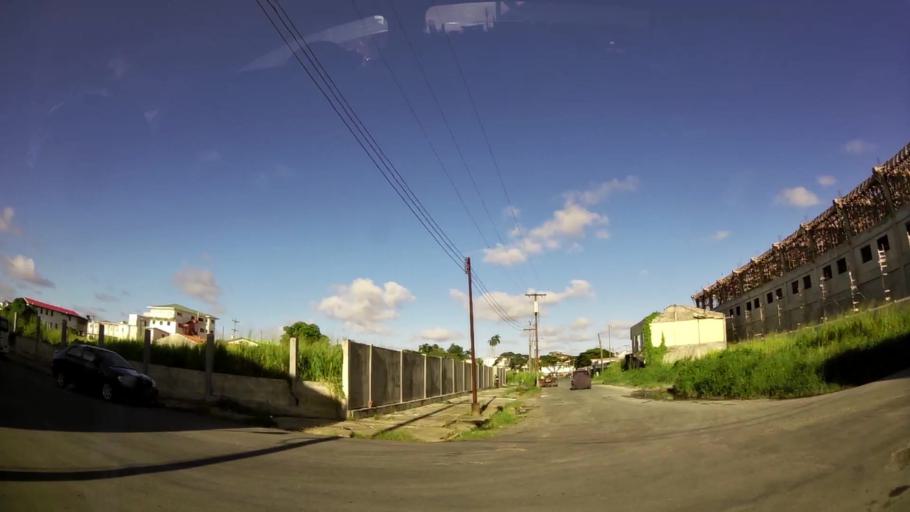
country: GY
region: Demerara-Mahaica
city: Georgetown
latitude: 6.8175
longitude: -58.1660
